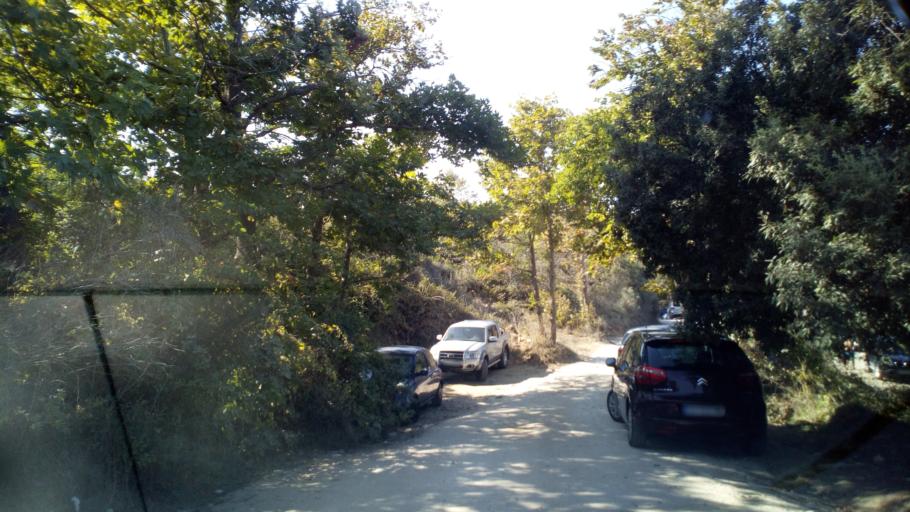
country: GR
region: Central Macedonia
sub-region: Nomos Chalkidikis
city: Stratonion
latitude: 40.5851
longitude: 23.7969
